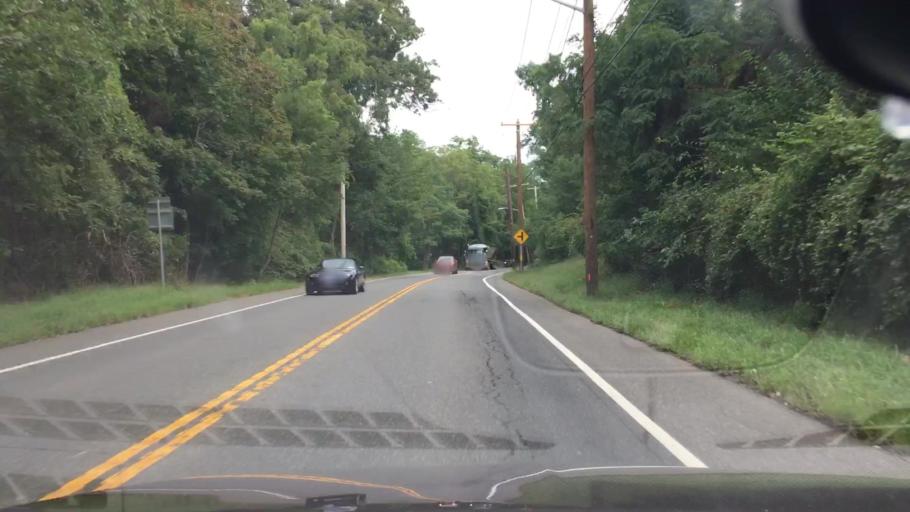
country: US
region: New York
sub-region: Suffolk County
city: Head of the Harbor
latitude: 40.9007
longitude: -73.1457
